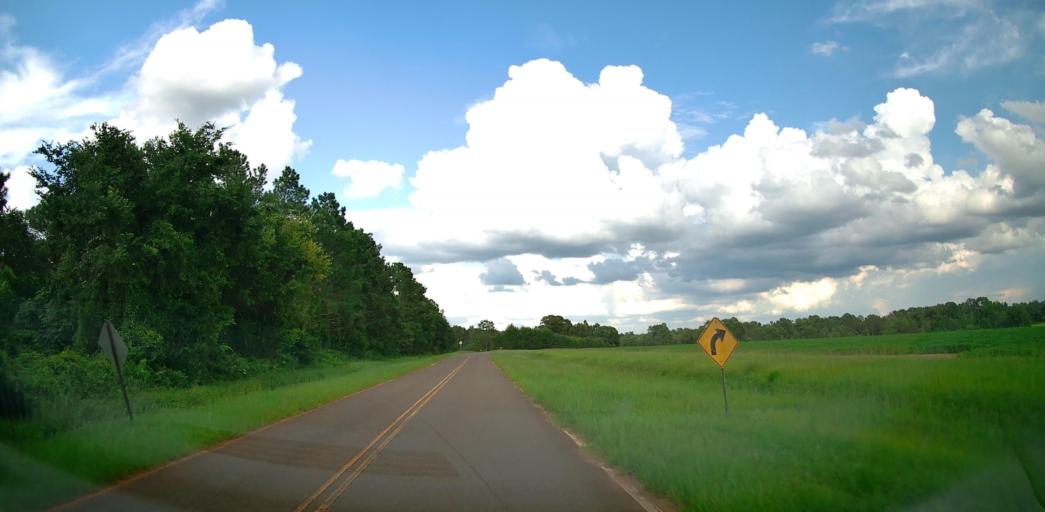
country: US
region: Georgia
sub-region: Bleckley County
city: Cochran
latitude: 32.4138
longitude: -83.4430
